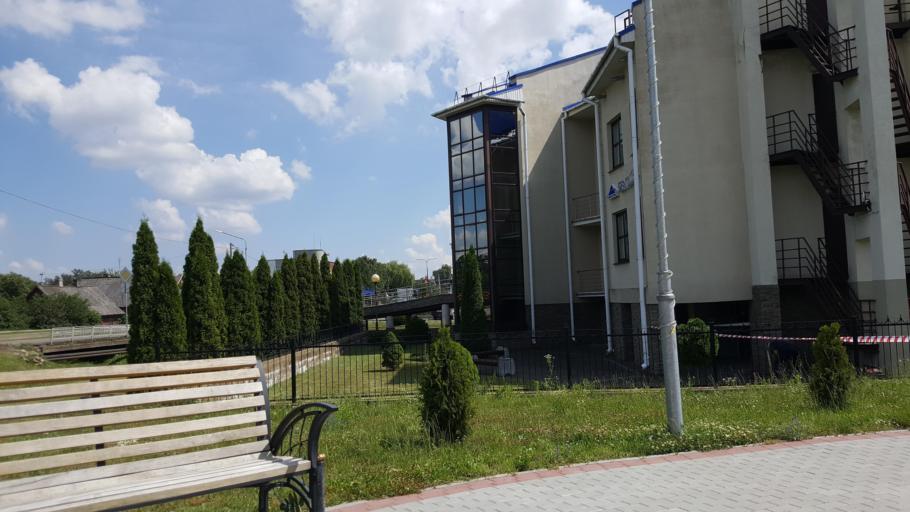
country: BY
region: Brest
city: Kamyanyets
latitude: 52.3987
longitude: 23.8245
